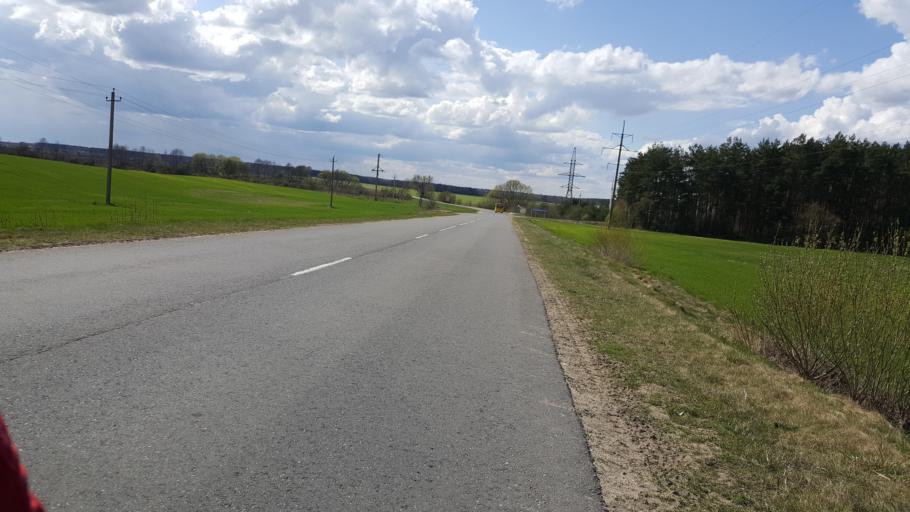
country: BY
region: Brest
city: Kamyanyets
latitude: 52.3803
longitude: 23.6593
